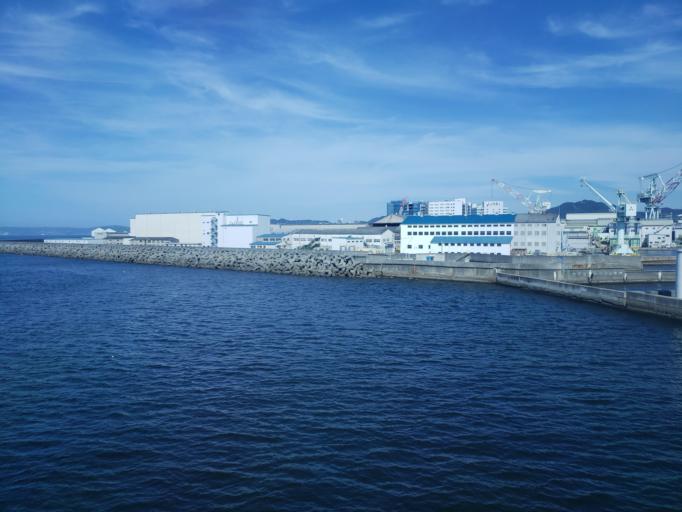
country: JP
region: Hyogo
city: Kobe
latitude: 34.6522
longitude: 135.1885
